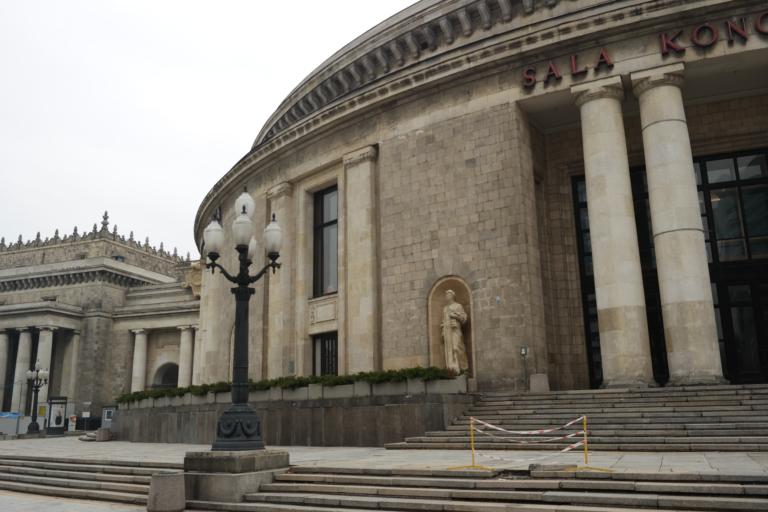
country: PL
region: Masovian Voivodeship
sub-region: Warszawa
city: Warsaw
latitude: 52.2317
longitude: 21.0040
